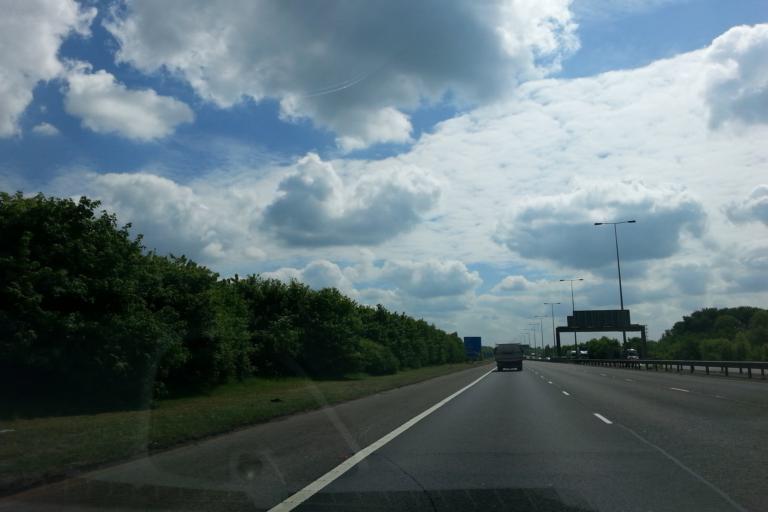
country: GB
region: England
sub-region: Cambridgeshire
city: Stilton
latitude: 52.5230
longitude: -0.3073
